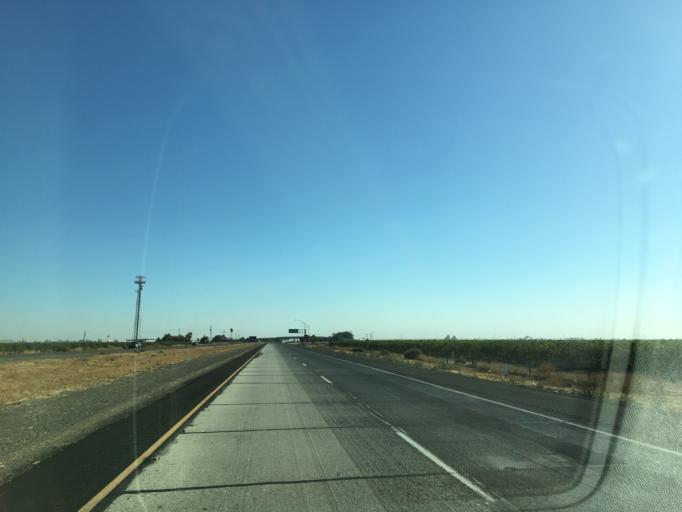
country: US
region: California
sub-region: Merced County
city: Dos Palos
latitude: 37.0797
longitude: -120.5022
